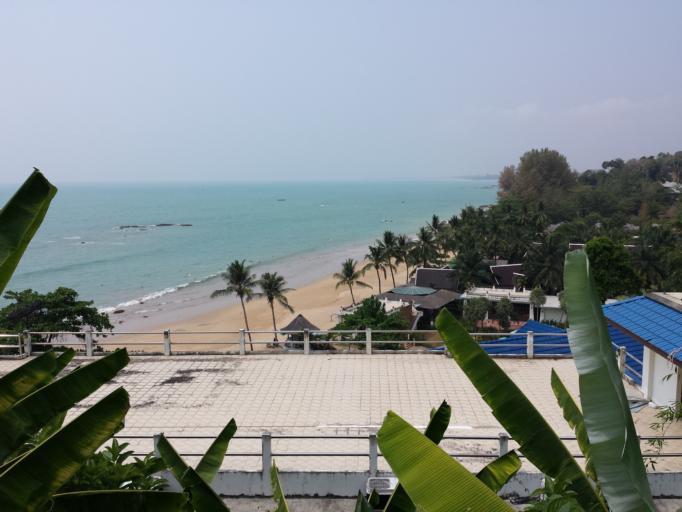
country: TH
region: Phangnga
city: Ban Khao Lak
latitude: 8.6291
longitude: 98.2442
